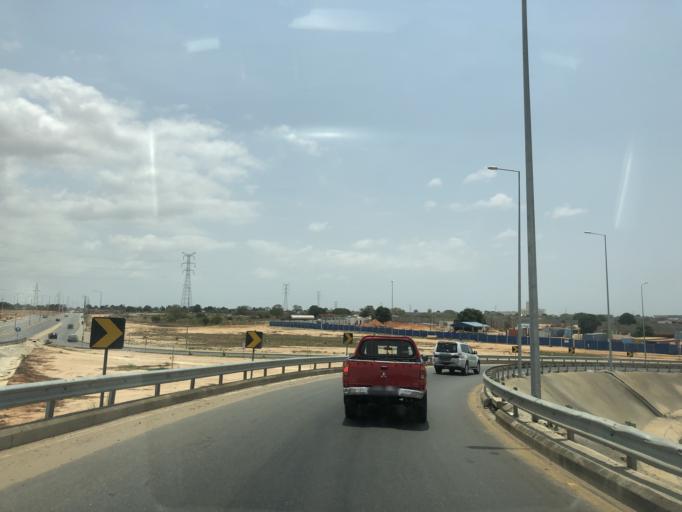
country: AO
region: Luanda
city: Luanda
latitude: -8.9747
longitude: 13.2533
